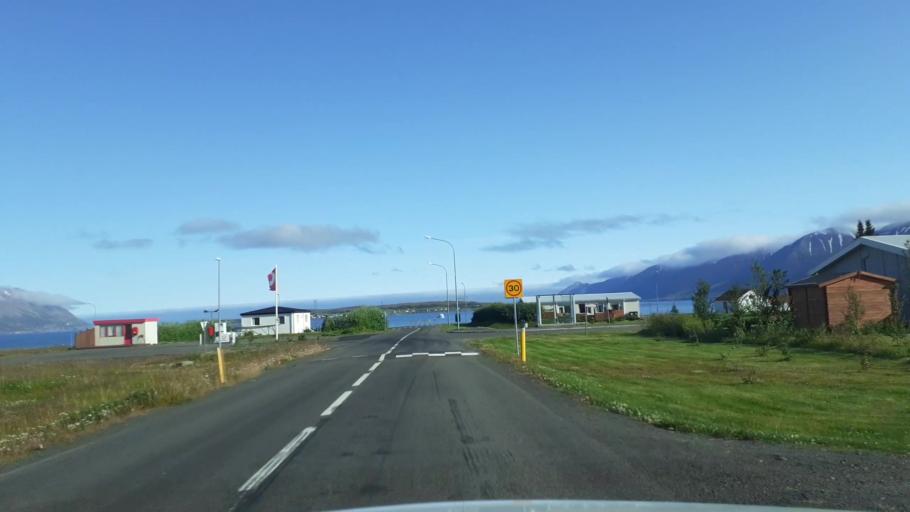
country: IS
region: Northeast
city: Dalvik
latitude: 65.9436
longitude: -18.3542
